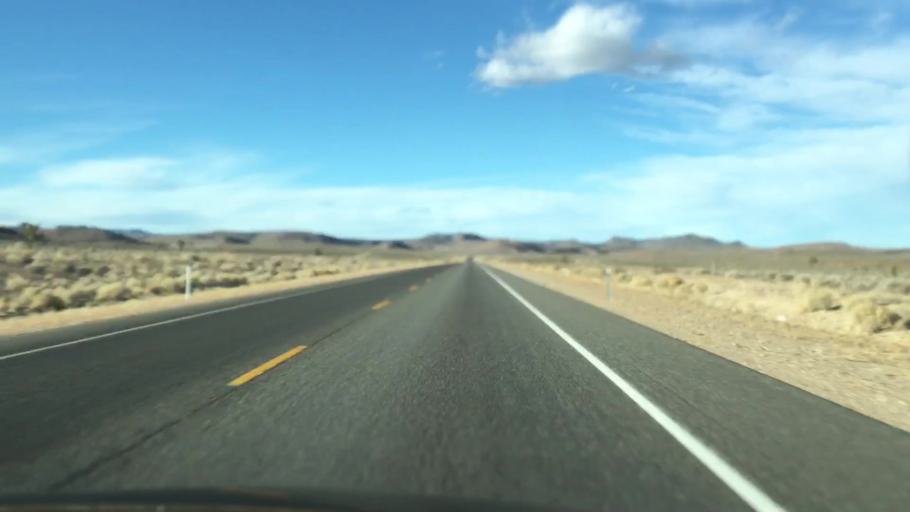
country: US
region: Nevada
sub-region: Esmeralda County
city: Goldfield
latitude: 37.5994
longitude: -117.2118
